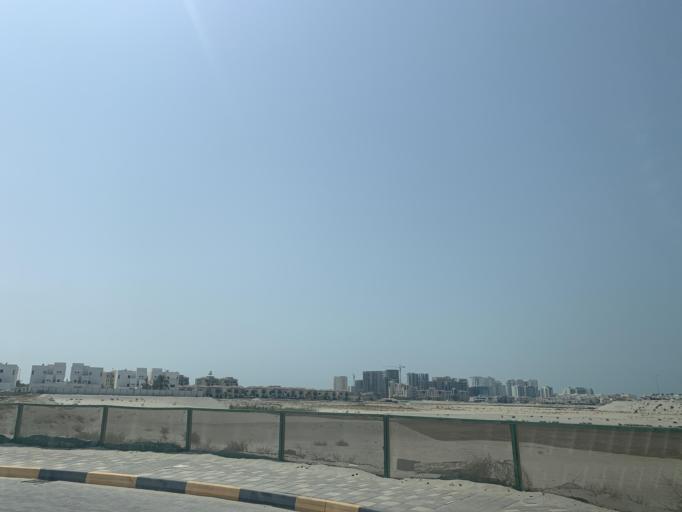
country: BH
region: Muharraq
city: Al Hadd
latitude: 26.2748
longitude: 50.6738
